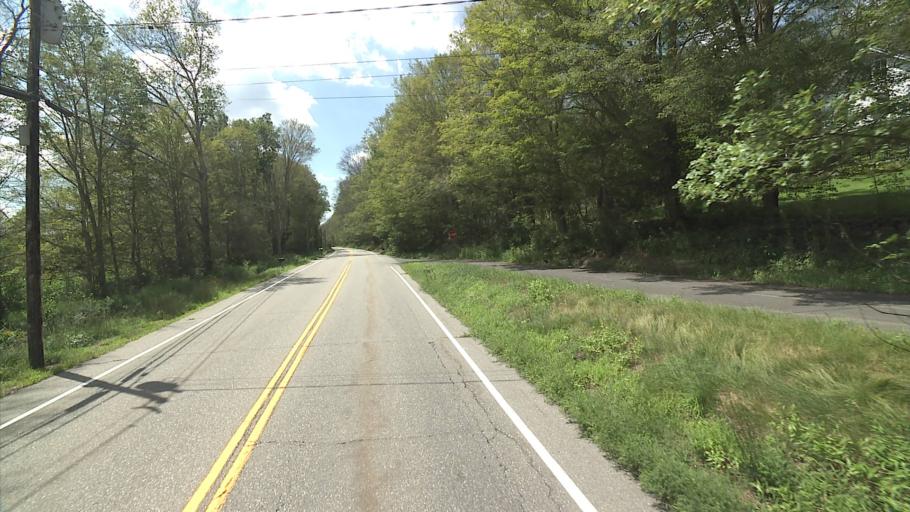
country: US
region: Connecticut
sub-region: Windham County
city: Windham
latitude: 41.8235
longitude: -72.1040
